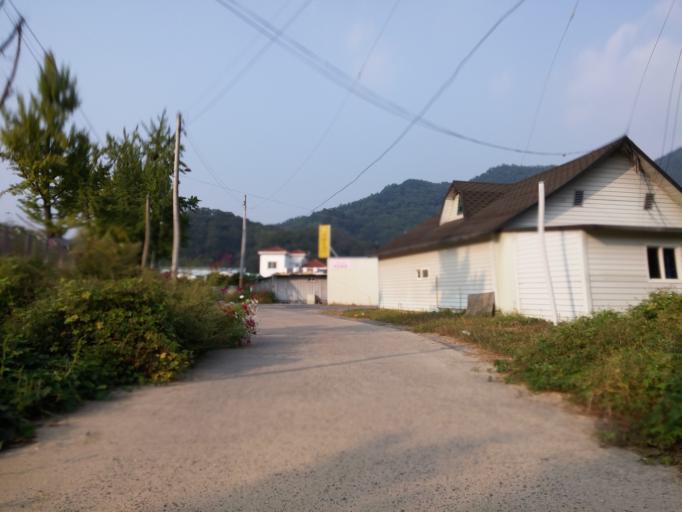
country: KR
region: Chungcheongbuk-do
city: Okcheon
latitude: 36.3329
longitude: 127.5239
